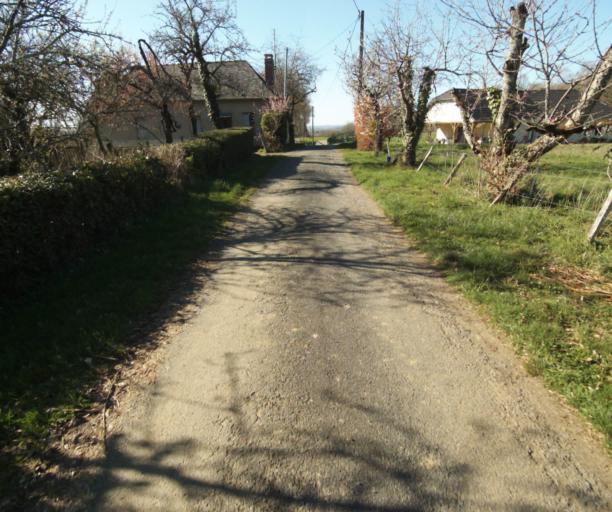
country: FR
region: Limousin
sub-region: Departement de la Correze
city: Chamboulive
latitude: 45.4059
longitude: 1.6595
